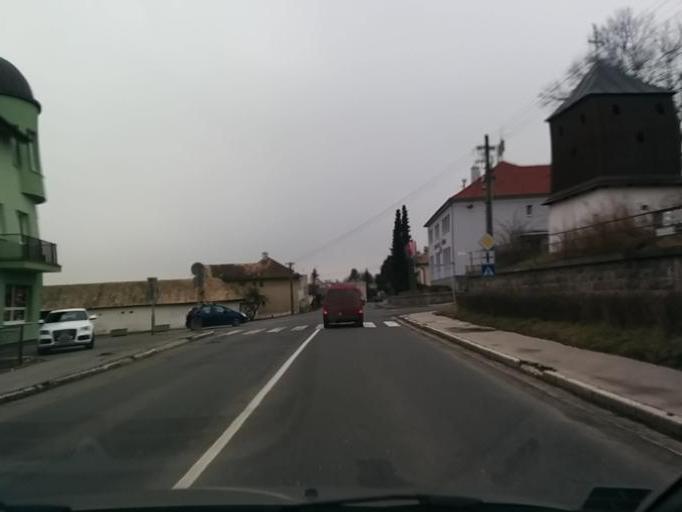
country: SK
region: Banskobystricky
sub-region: Okres Banska Bystrica
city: Zvolen
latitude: 48.6168
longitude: 19.1365
